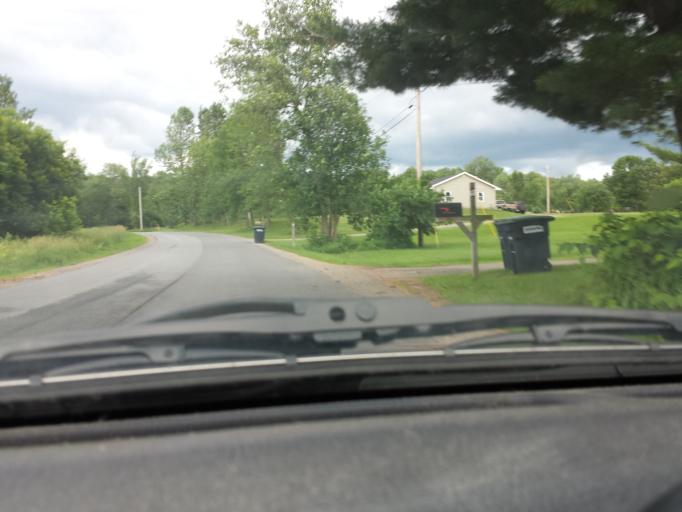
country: US
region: New York
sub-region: St. Lawrence County
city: Norwood
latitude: 44.7120
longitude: -74.9807
